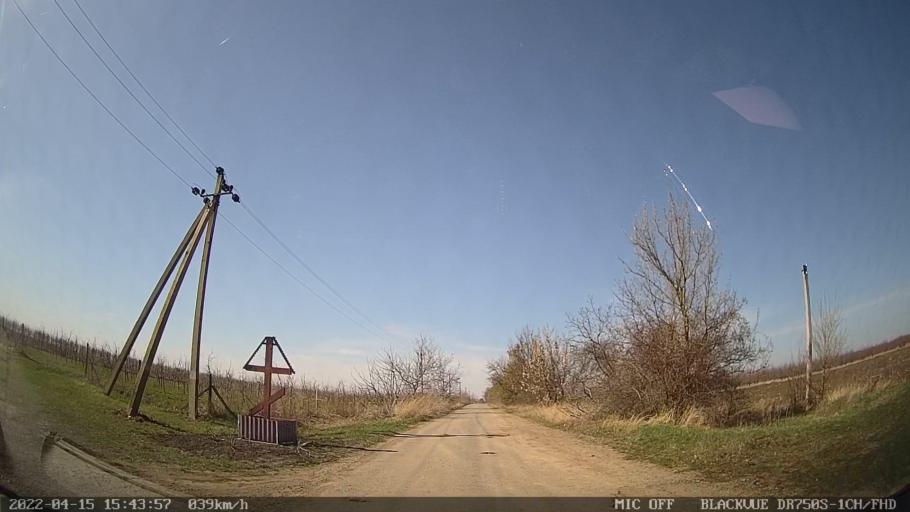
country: MD
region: Raionul Ocnita
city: Otaci
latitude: 48.3676
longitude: 27.9244
